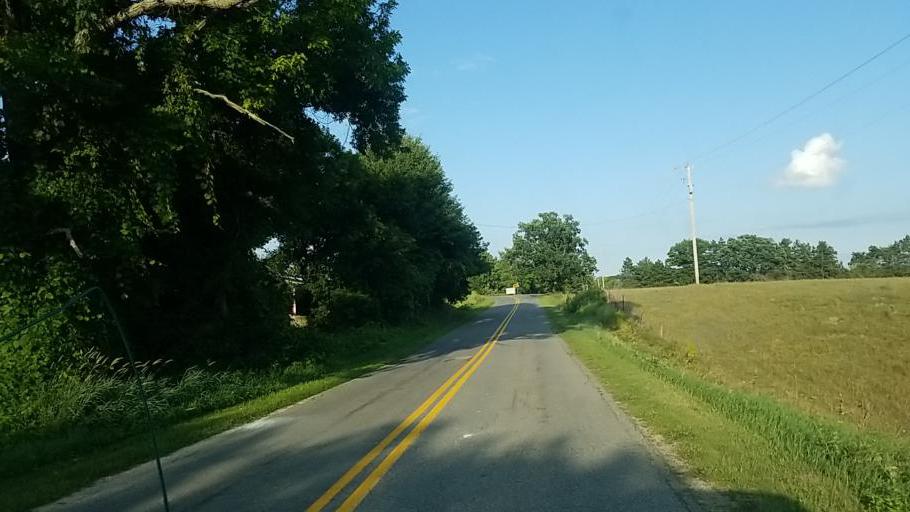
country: US
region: Michigan
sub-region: Montcalm County
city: Greenville
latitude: 43.2644
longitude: -85.3654
